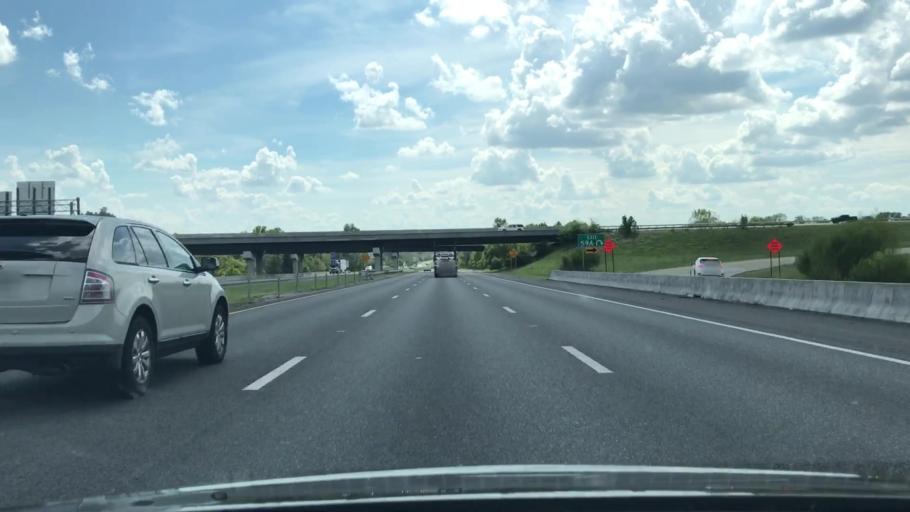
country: US
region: Tennessee
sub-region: Williamson County
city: Thompson's Station
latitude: 35.8203
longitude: -86.8398
